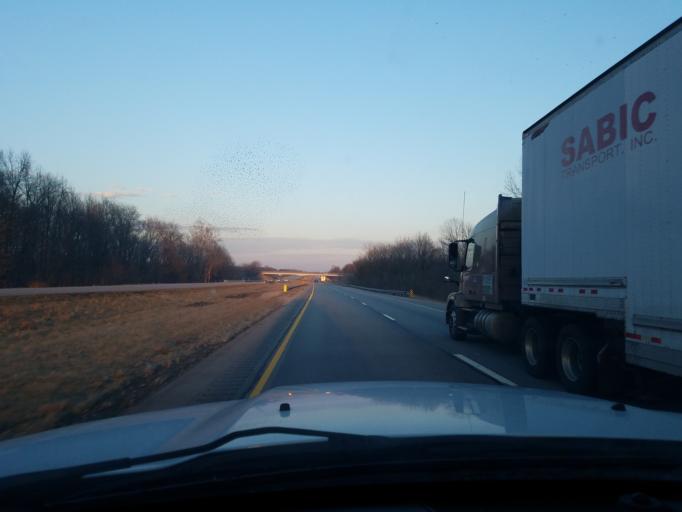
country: US
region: Indiana
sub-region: Warrick County
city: Chandler
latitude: 38.1861
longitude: -87.3592
